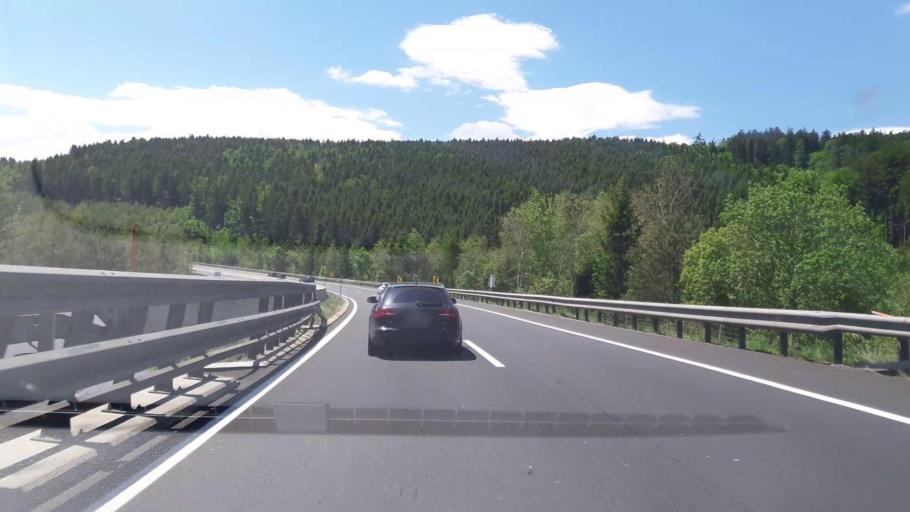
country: AT
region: Lower Austria
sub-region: Politischer Bezirk Neunkirchen
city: Zobern
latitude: 47.4948
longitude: 16.0986
